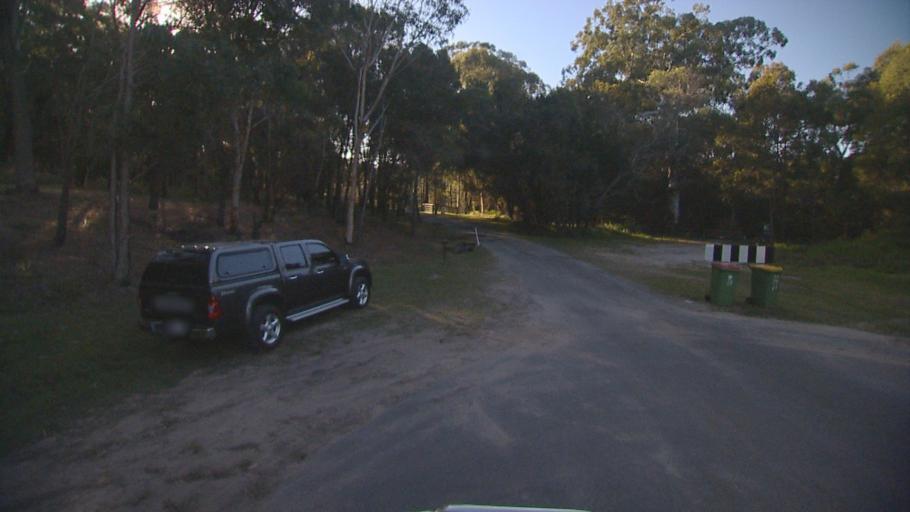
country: AU
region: Queensland
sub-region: Redland
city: Redland Bay
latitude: -27.6579
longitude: 153.2743
